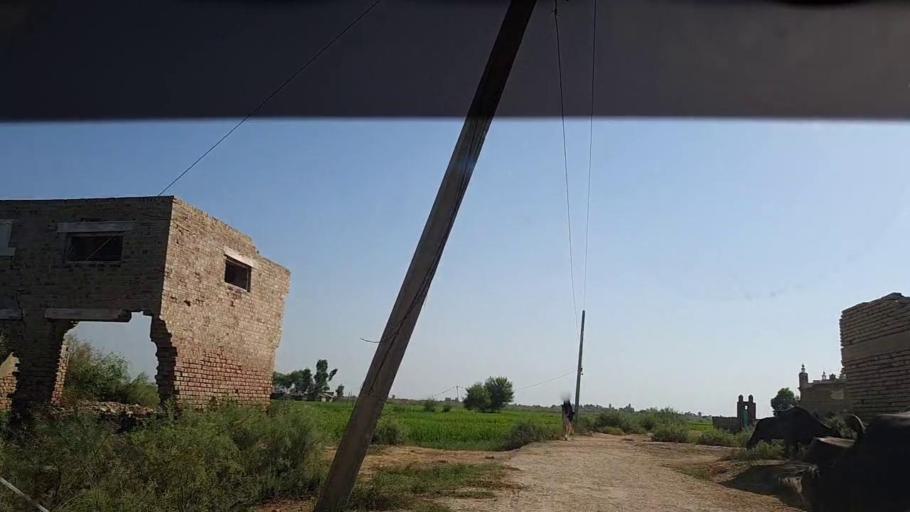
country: PK
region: Sindh
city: Ghauspur
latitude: 28.1782
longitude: 69.0285
